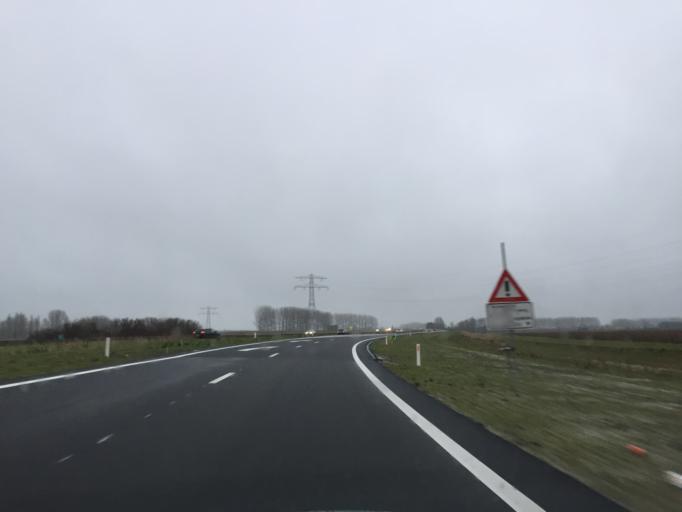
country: NL
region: Zeeland
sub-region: Gemeente Borsele
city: Borssele
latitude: 51.4862
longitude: 3.7984
